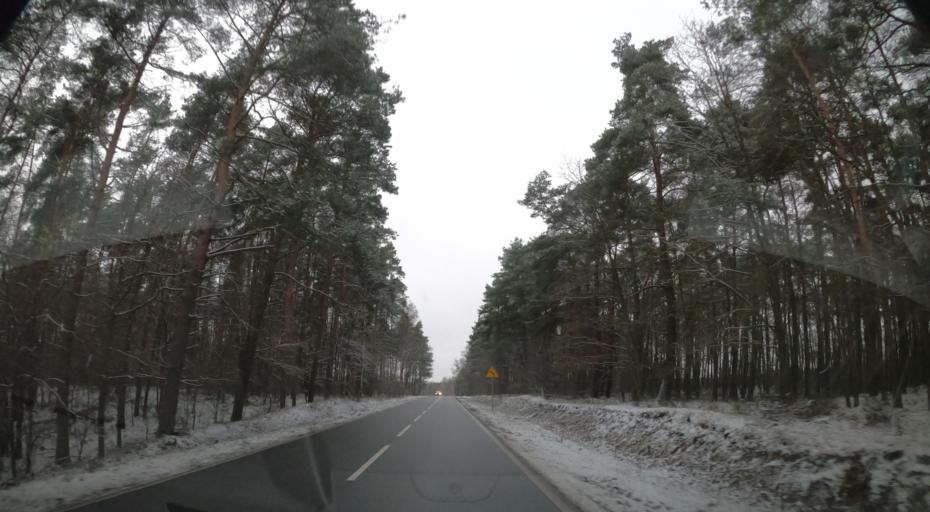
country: PL
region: Kujawsko-Pomorskie
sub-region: Powiat lipnowski
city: Wielgie
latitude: 52.7605
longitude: 19.2318
